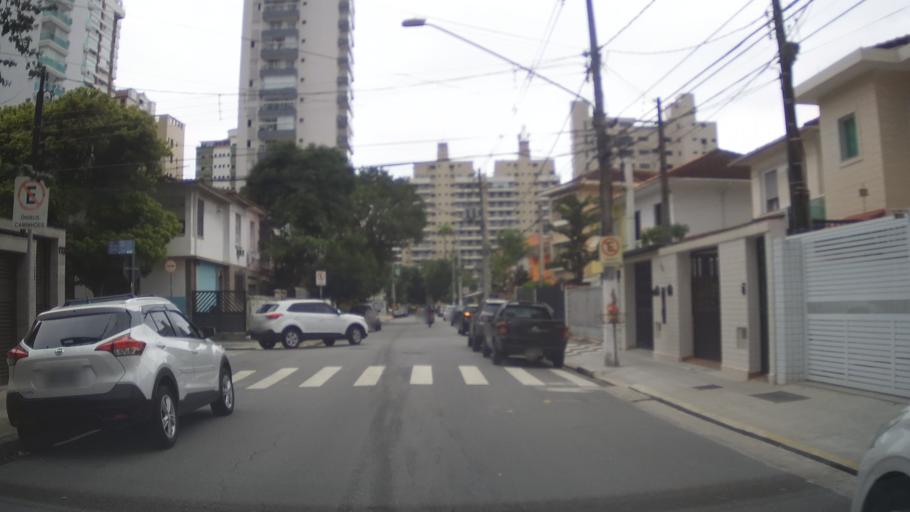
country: BR
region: Sao Paulo
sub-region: Santos
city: Santos
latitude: -23.9700
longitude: -46.3191
